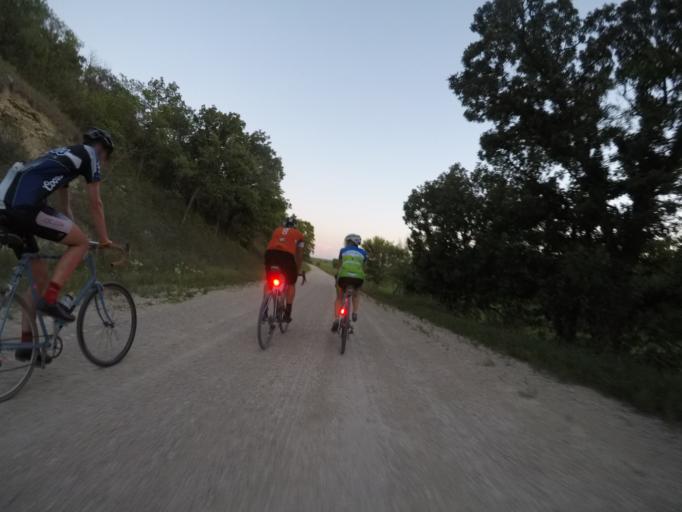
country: US
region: Kansas
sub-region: Riley County
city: Ogden
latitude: 38.9789
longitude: -96.5636
